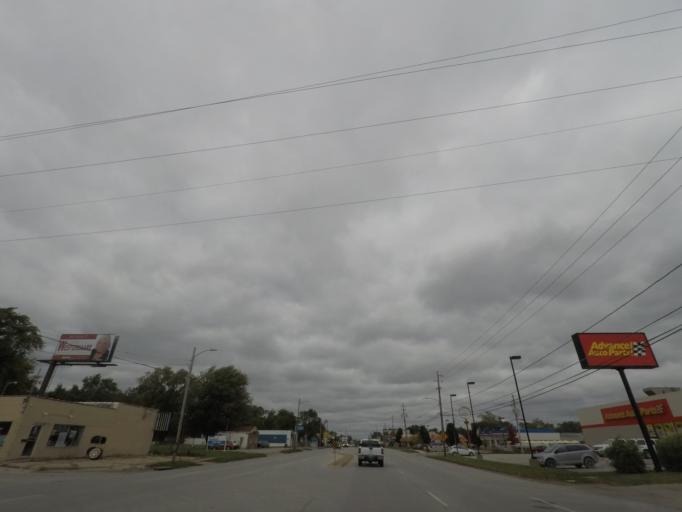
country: US
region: Iowa
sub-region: Polk County
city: Des Moines
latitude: 41.6294
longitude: -93.6005
